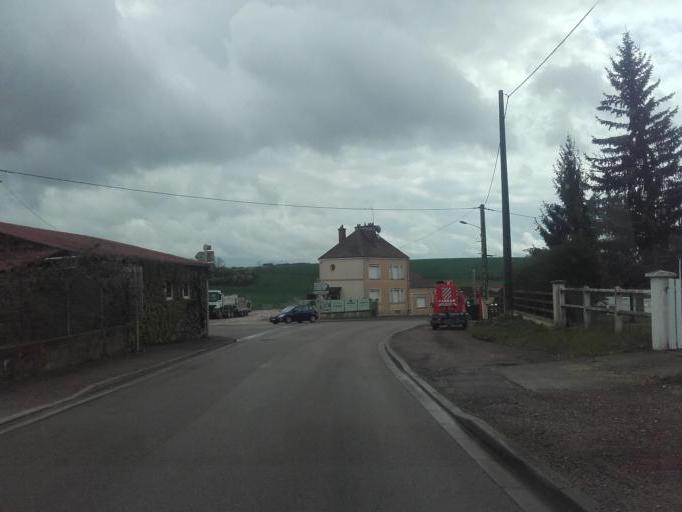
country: FR
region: Bourgogne
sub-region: Departement de l'Yonne
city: Chablis
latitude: 47.8088
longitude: 3.7985
